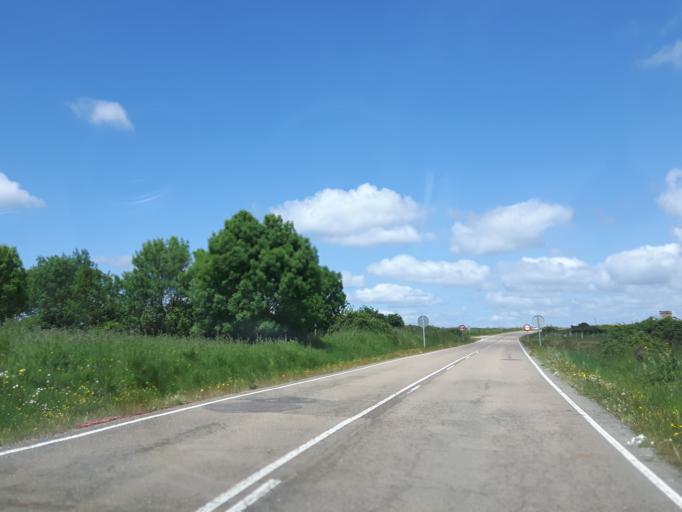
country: ES
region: Castille and Leon
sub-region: Provincia de Salamanca
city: Villar de la Yegua
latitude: 40.7257
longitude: -6.7087
